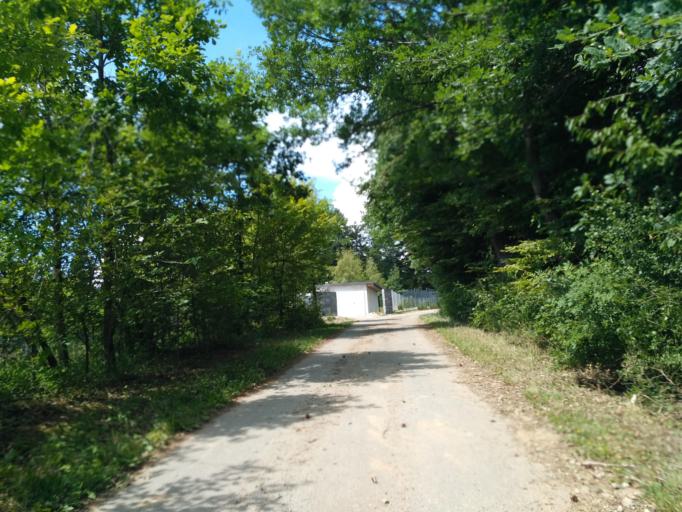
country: PL
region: Subcarpathian Voivodeship
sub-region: Powiat jasielski
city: Brzyska
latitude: 49.8015
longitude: 21.3771
